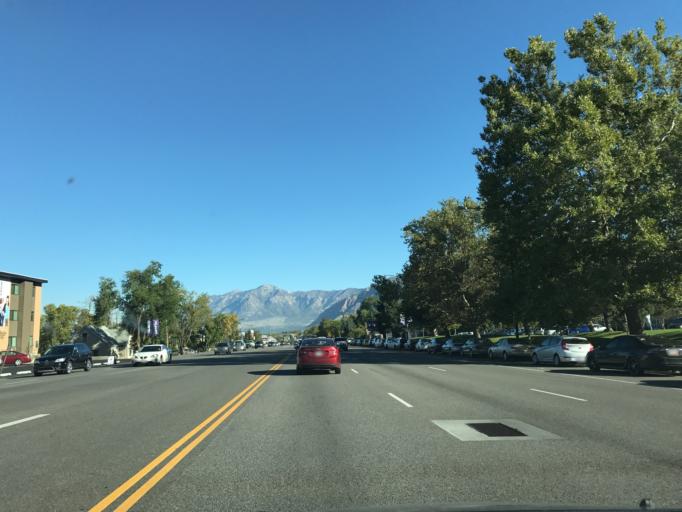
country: US
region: Utah
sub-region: Weber County
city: South Ogden
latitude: 41.1942
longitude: -111.9487
